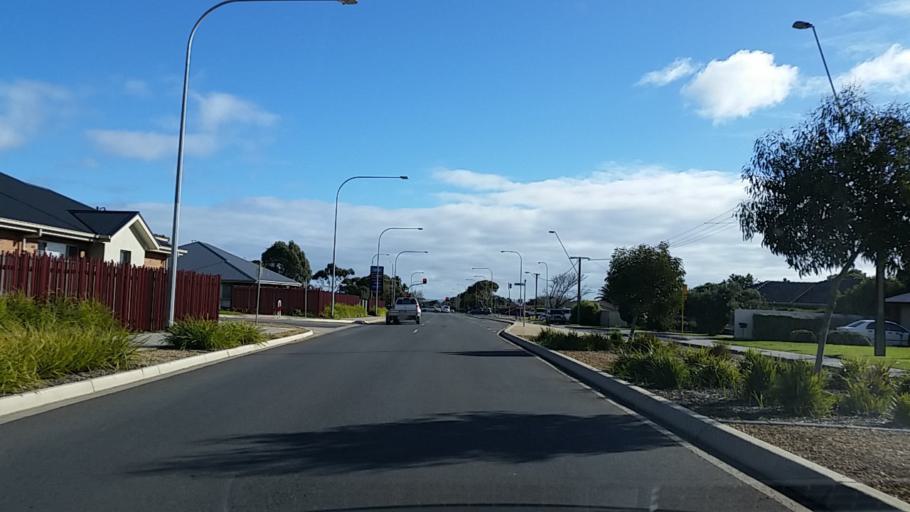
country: AU
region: South Australia
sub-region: Onkaparinga
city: Noarlunga
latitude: -35.1906
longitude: 138.4922
